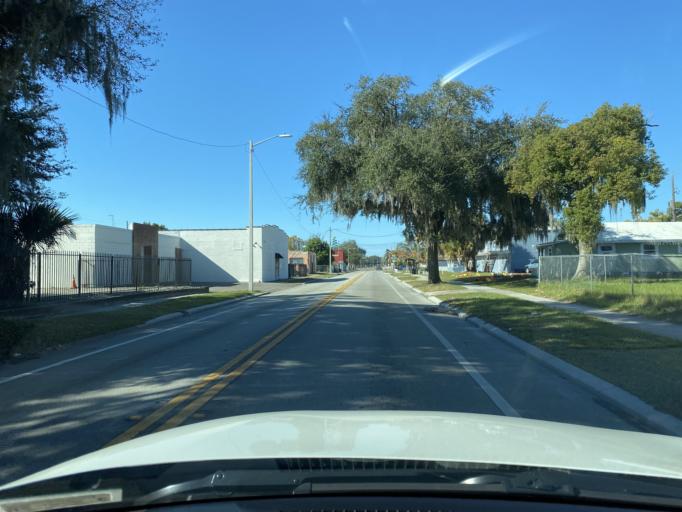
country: US
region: Florida
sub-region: Orange County
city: Orlando
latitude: 28.5439
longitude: -81.3942
